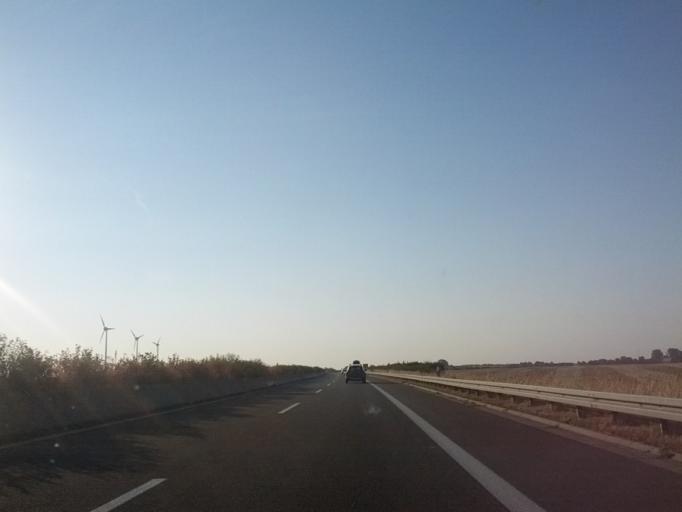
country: DE
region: Mecklenburg-Vorpommern
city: Brandshagen
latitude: 54.2447
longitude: 13.1363
